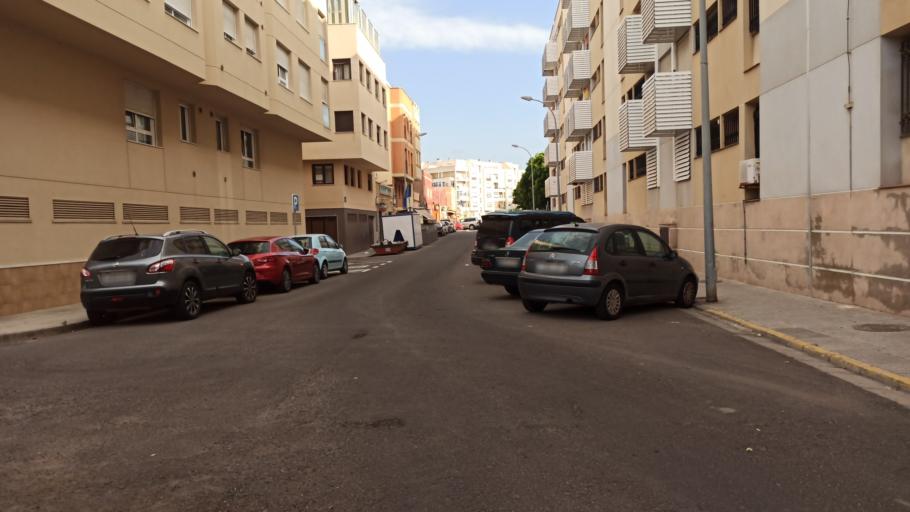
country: ES
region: Melilla
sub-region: Melilla
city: Melilla
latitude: 35.2845
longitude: -2.9513
